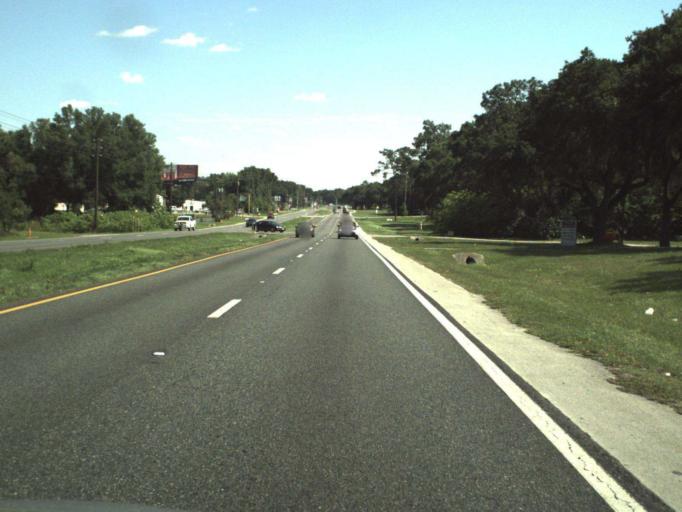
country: US
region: Florida
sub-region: Marion County
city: Belleview
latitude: 29.1186
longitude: -82.0985
